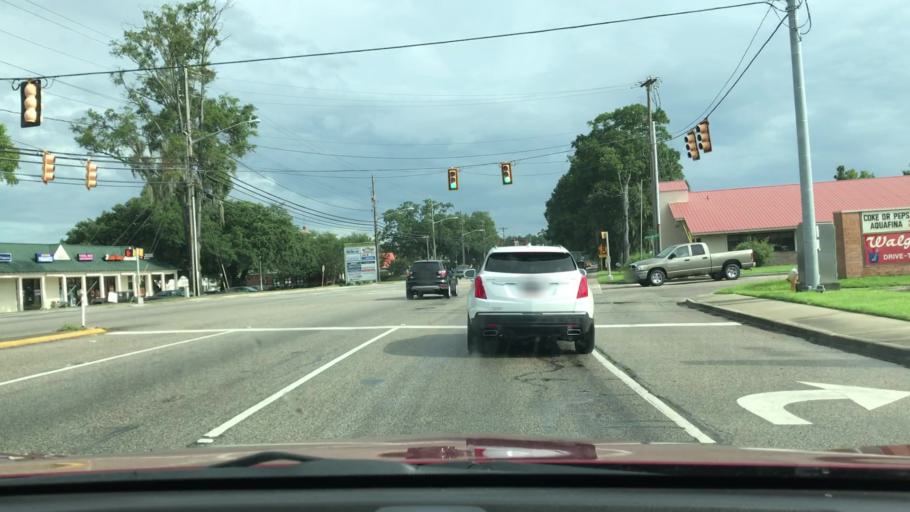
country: US
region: South Carolina
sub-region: Georgetown County
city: Georgetown
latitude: 33.3874
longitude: -79.2889
